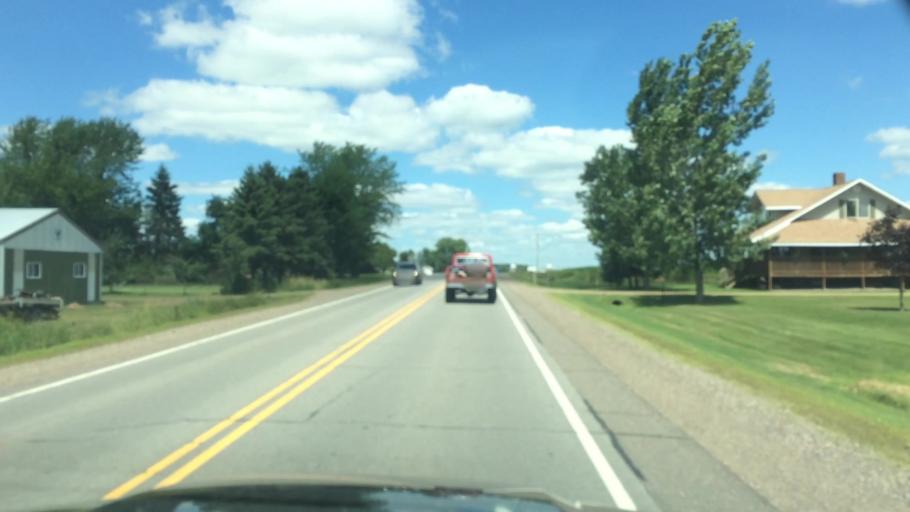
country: US
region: Wisconsin
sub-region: Taylor County
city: Medford
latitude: 45.0824
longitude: -90.3147
